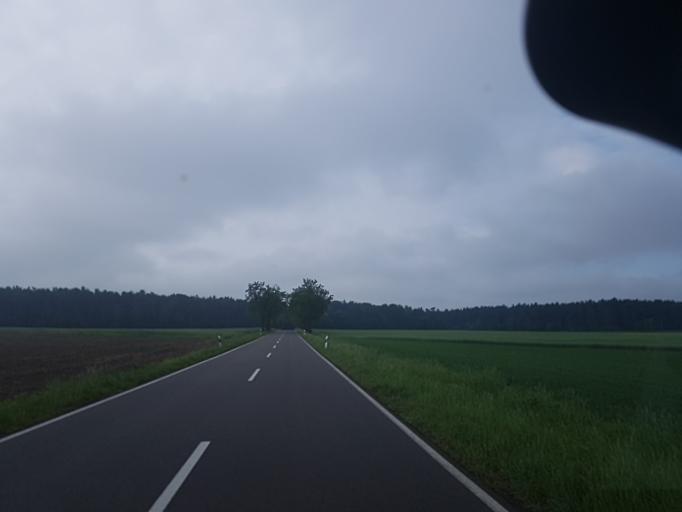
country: DE
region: Saxony-Anhalt
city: Klieken
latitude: 52.0040
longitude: 12.3703
